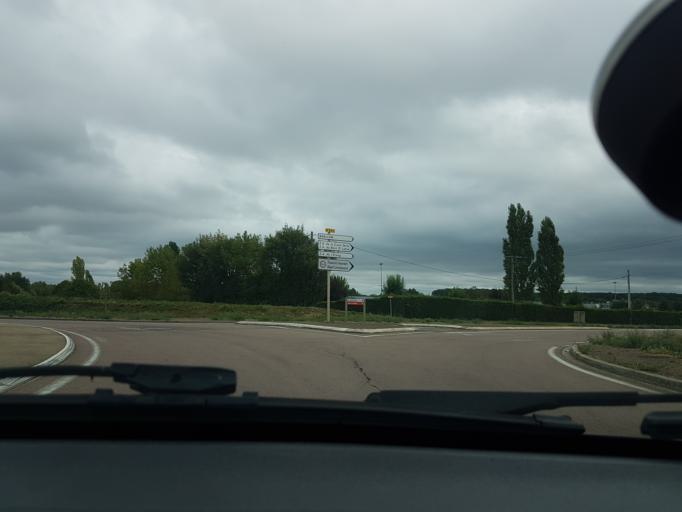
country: FR
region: Bourgogne
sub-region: Departement de l'Yonne
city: Avallon
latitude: 47.5001
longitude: 3.9275
